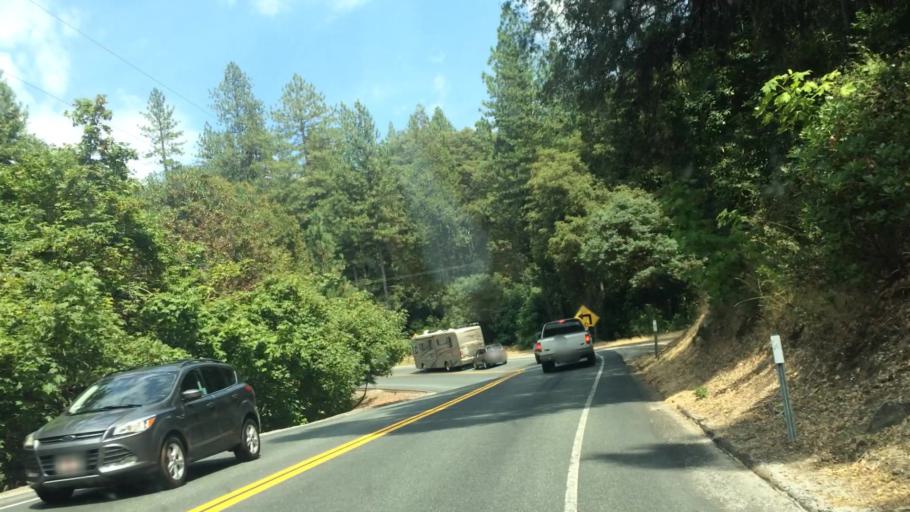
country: US
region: California
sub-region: Amador County
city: Pioneer
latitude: 38.4202
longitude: -120.6018
